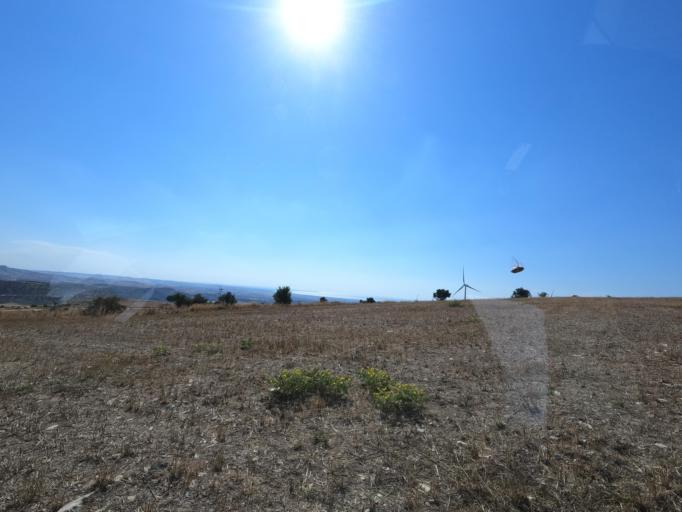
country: CY
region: Larnaka
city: Psevdas
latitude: 34.9701
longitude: 33.4837
